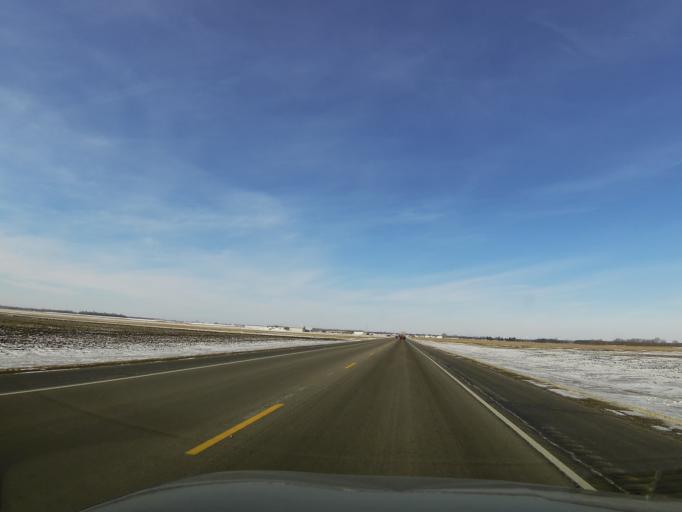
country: US
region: North Dakota
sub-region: Walsh County
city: Grafton
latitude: 48.4125
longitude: -97.3593
